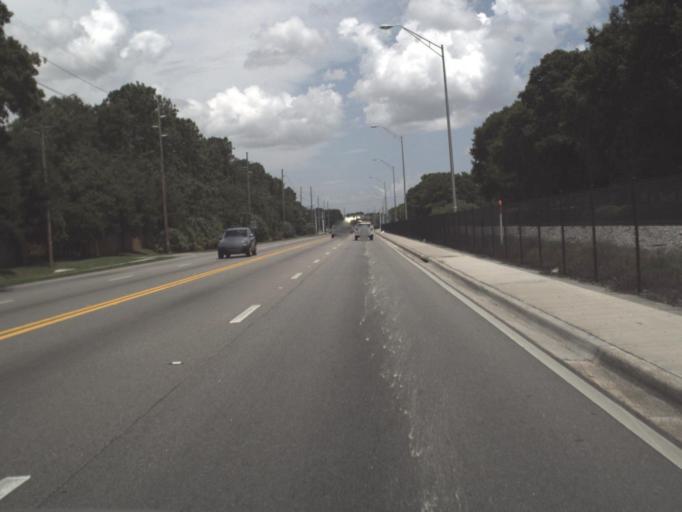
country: US
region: Florida
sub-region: Hillsborough County
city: Carrollwood
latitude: 28.0361
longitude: -82.4968
